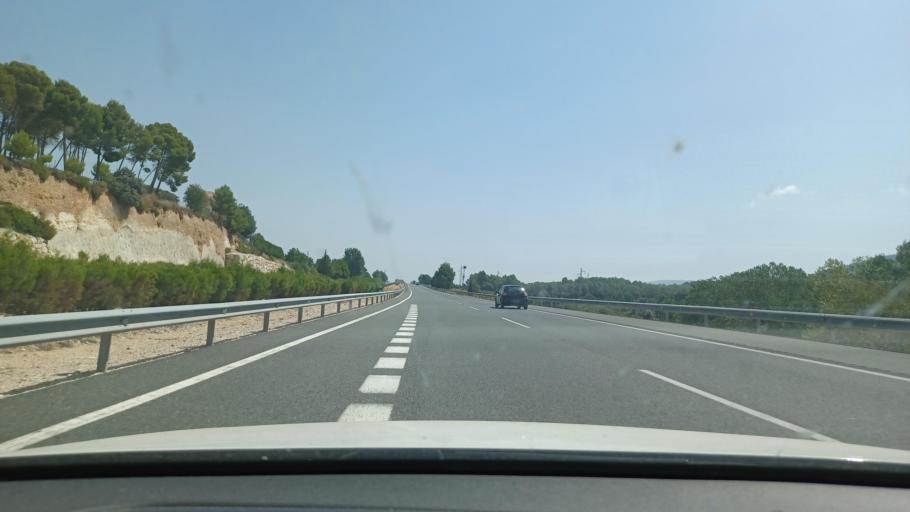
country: ES
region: Valencia
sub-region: Provincia de Alicante
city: Ibi
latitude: 38.6322
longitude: -0.5207
